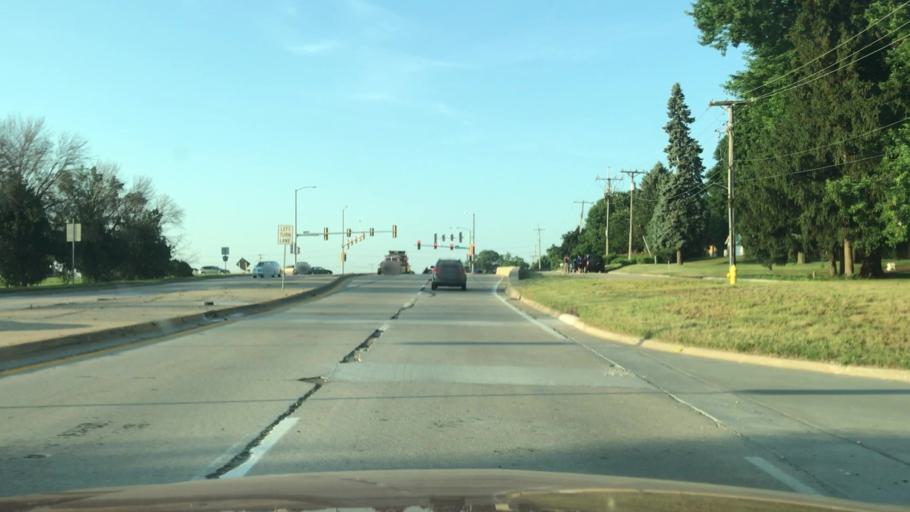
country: US
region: Illinois
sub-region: Winnebago County
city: Cherry Valley
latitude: 42.2415
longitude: -88.9799
